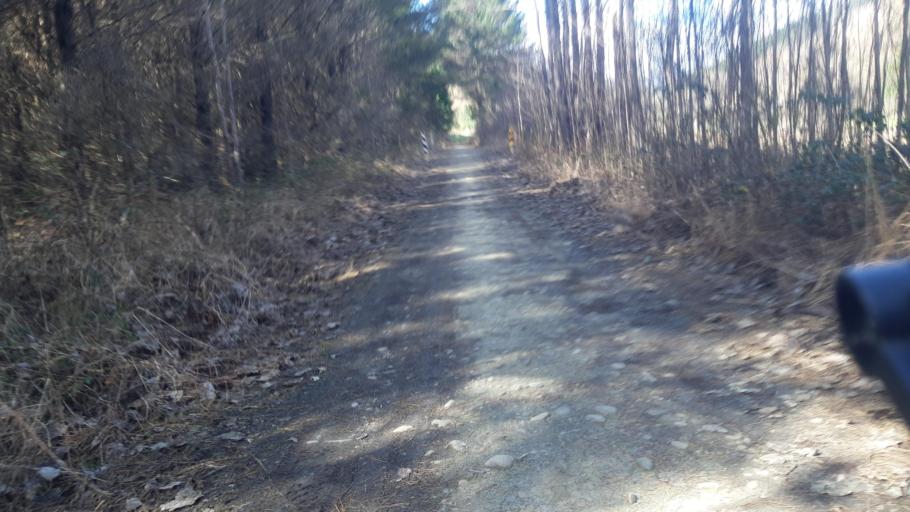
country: NZ
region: Tasman
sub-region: Tasman District
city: Wakefield
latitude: -41.4825
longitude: 172.8842
